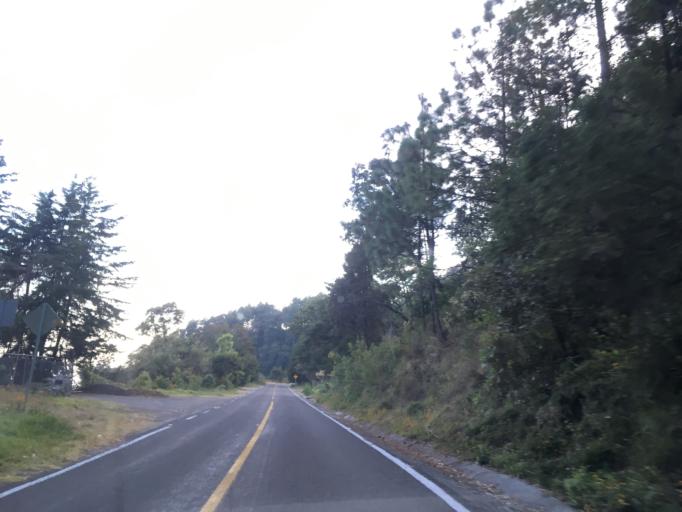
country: MX
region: Michoacan
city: Tzitzio
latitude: 19.6679
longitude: -100.9241
